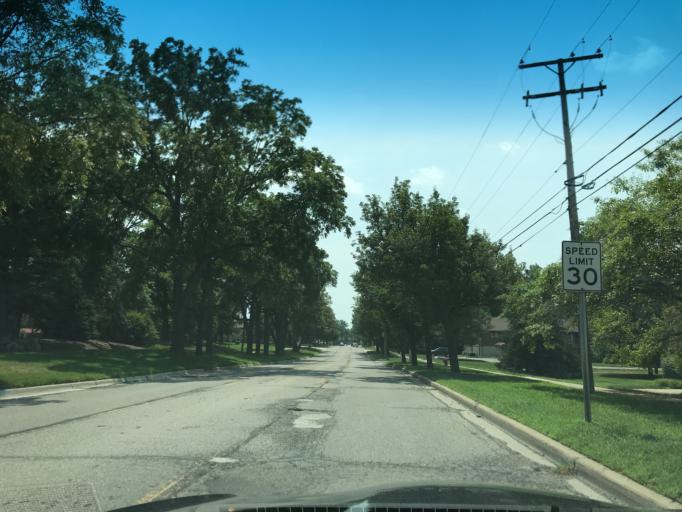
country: US
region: Michigan
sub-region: Oakland County
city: Bingham Farms
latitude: 42.4830
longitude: -83.2796
